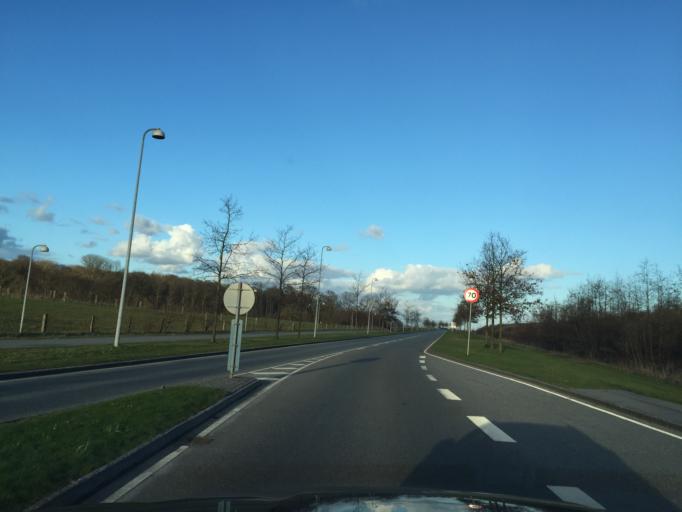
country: DK
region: South Denmark
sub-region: Odense Kommune
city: Neder Holluf
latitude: 55.3751
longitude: 10.4689
